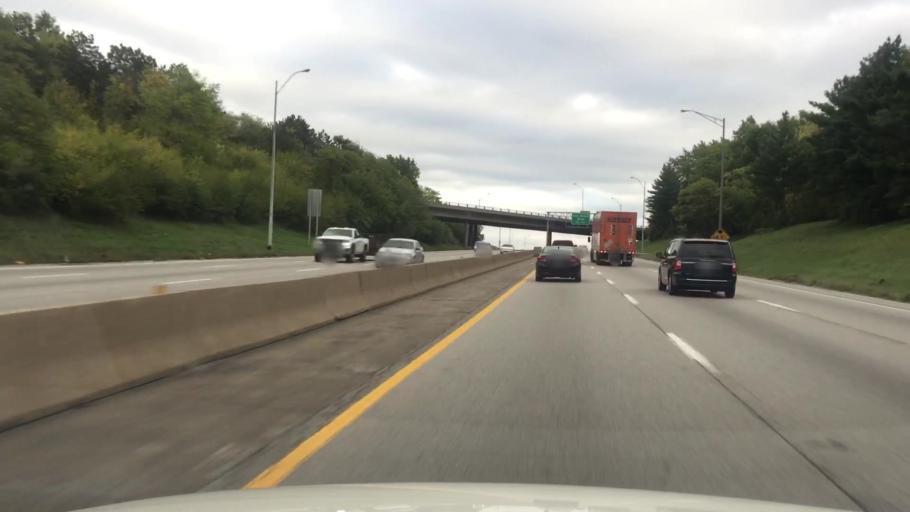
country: US
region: Missouri
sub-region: Jackson County
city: Kansas City
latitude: 39.0808
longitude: -94.5399
